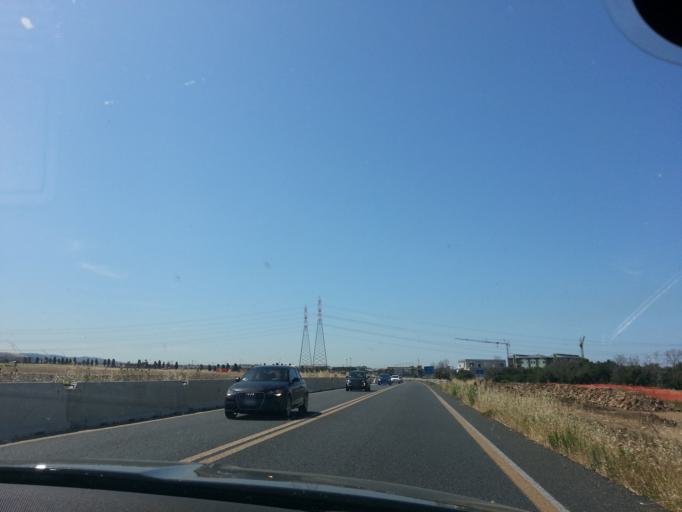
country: IT
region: Latium
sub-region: Citta metropolitana di Roma Capitale
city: Aurelia
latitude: 42.1720
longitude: 11.7876
